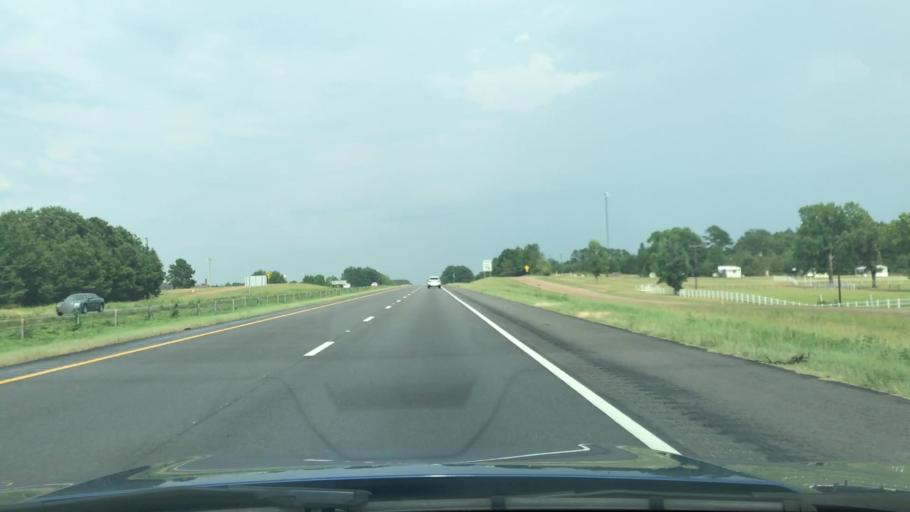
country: US
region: Texas
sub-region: Harrison County
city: Hallsville
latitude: 32.4754
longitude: -94.5699
